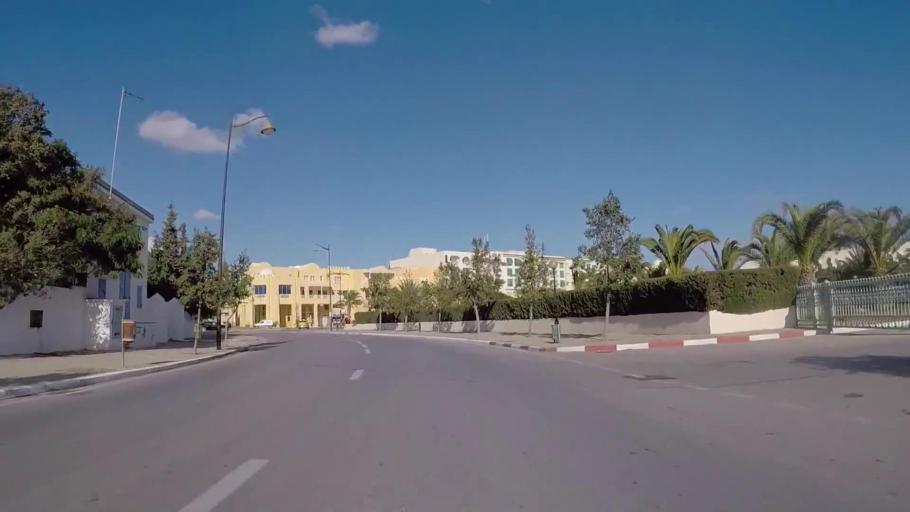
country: TN
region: Nabul
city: Al Hammamat
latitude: 36.3621
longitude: 10.5331
